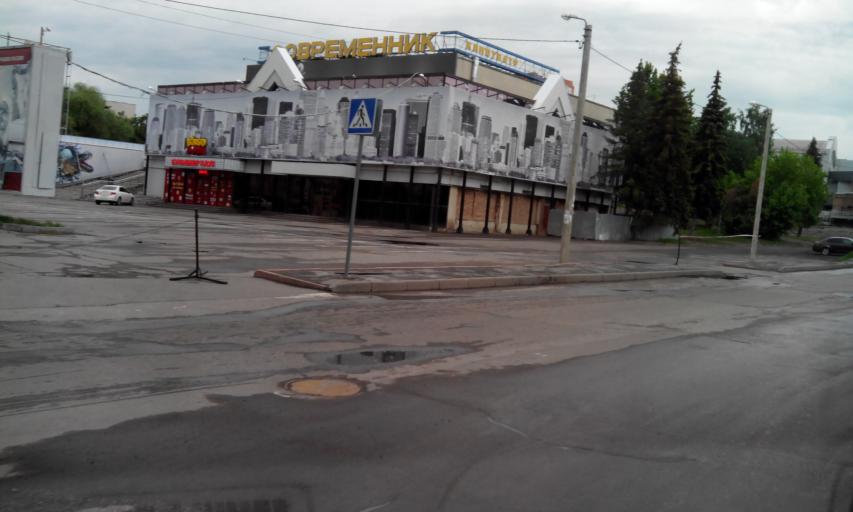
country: RU
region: Penza
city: Penza
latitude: 53.1958
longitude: 45.0088
